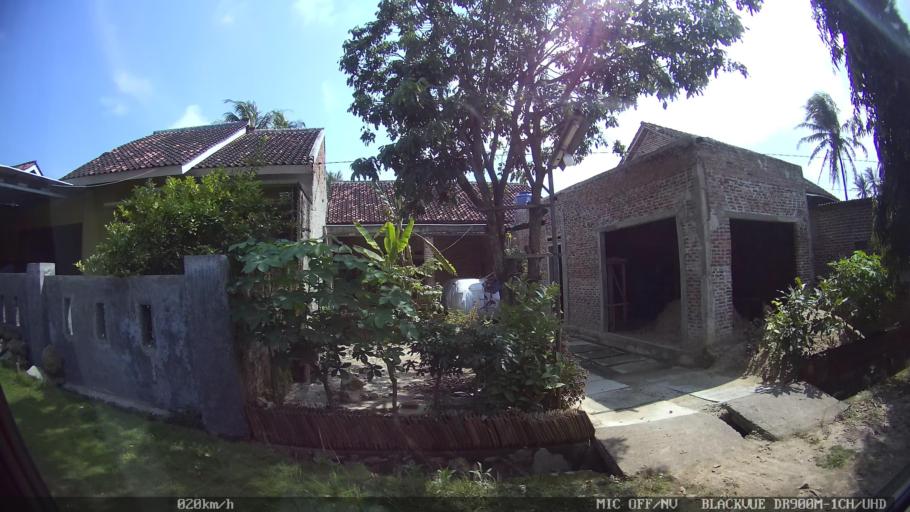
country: ID
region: Lampung
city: Kedaton
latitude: -5.3289
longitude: 105.2764
